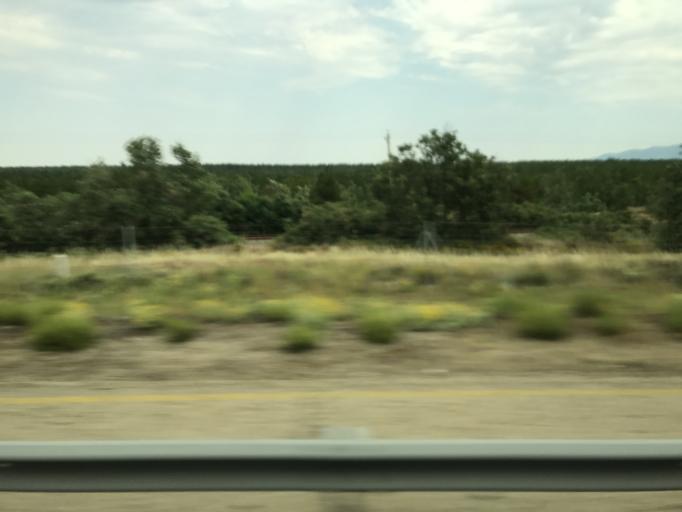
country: ES
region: Castille and Leon
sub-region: Provincia de Segovia
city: Castillejo de Mesleon
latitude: 41.2998
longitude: -3.6041
